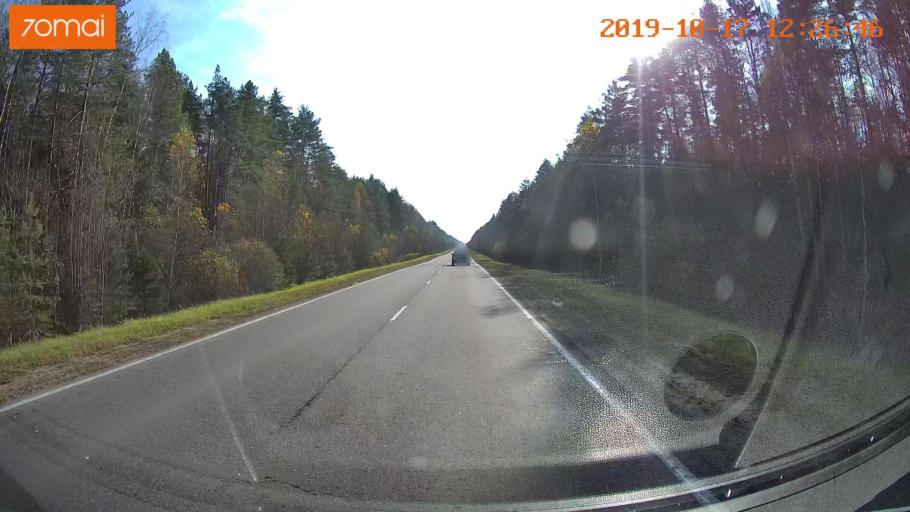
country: RU
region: Rjazan
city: Syntul
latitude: 55.0147
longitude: 41.2583
